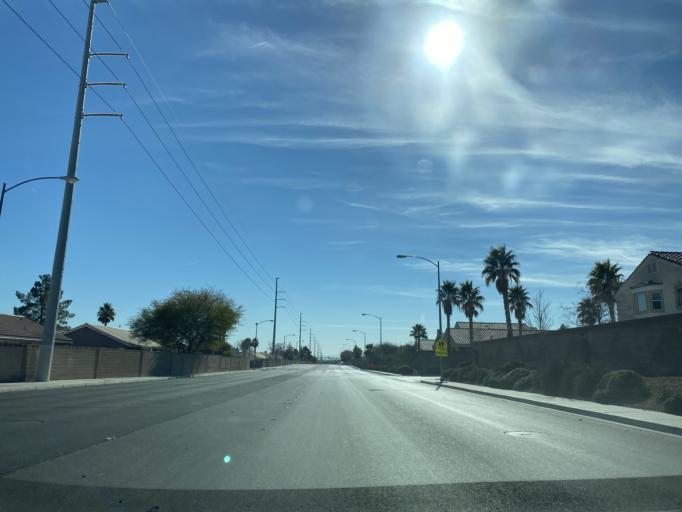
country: US
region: Nevada
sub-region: Clark County
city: North Las Vegas
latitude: 36.2590
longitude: -115.1440
